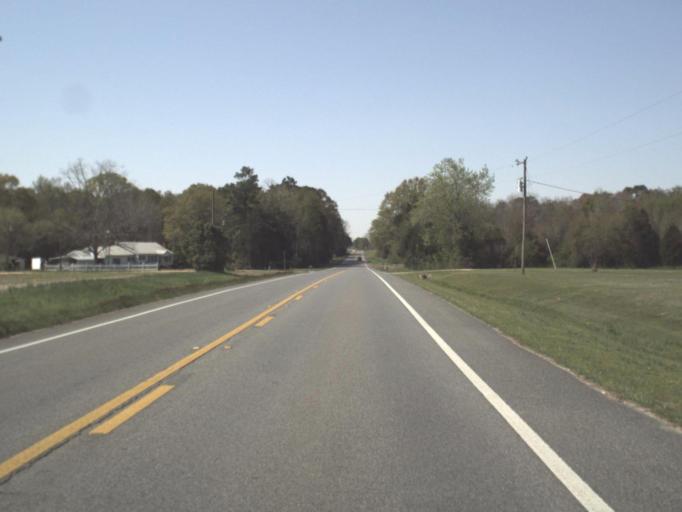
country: US
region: Florida
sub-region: Jackson County
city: Graceville
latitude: 30.8855
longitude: -85.4717
